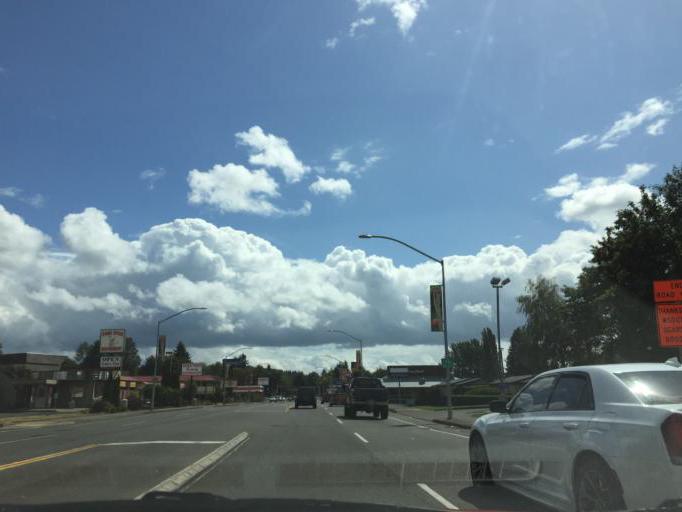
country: US
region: Washington
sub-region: Lewis County
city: Fords Prairie
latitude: 46.7250
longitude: -122.9732
